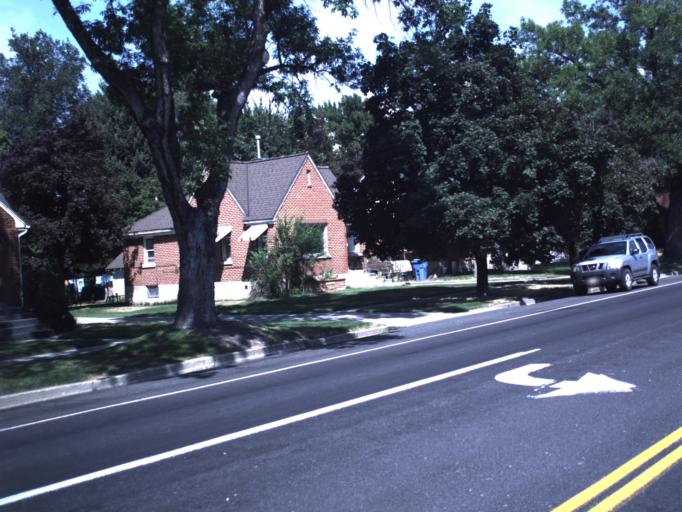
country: US
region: Utah
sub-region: Cache County
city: Logan
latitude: 41.7353
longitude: -111.8424
